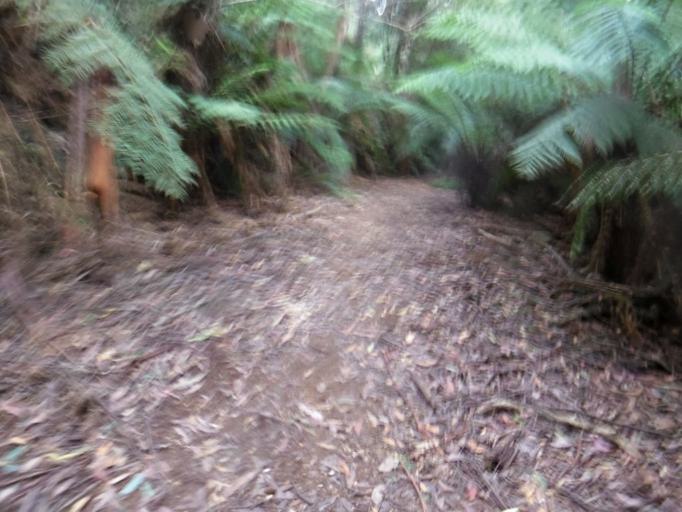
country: AU
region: Victoria
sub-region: Yarra Ranges
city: Healesville
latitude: -37.5182
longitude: 145.5207
